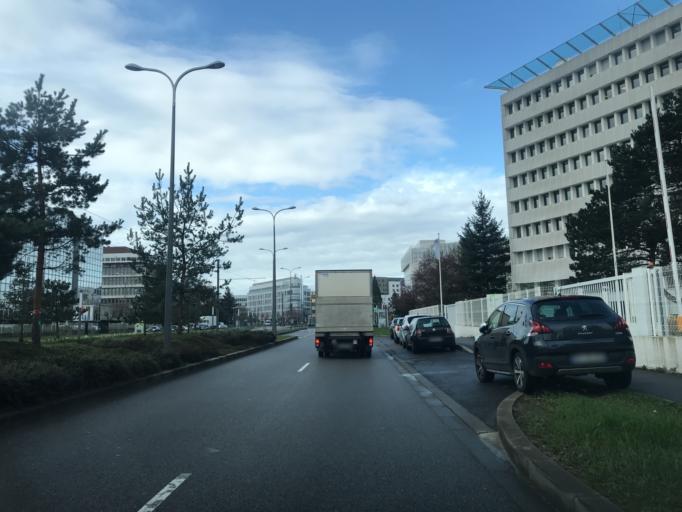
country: FR
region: Ile-de-France
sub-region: Departement des Yvelines
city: Velizy-Villacoublay
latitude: 48.7824
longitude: 2.2112
